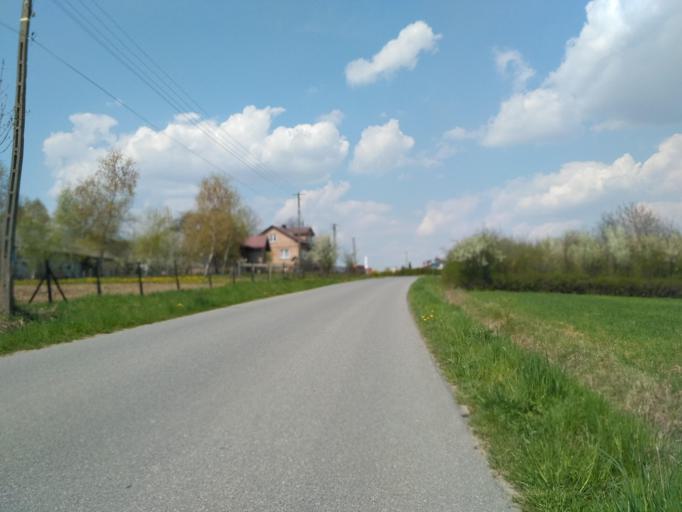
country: PL
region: Subcarpathian Voivodeship
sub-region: Powiat jasielski
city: Debowiec
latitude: 49.6963
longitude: 21.5091
